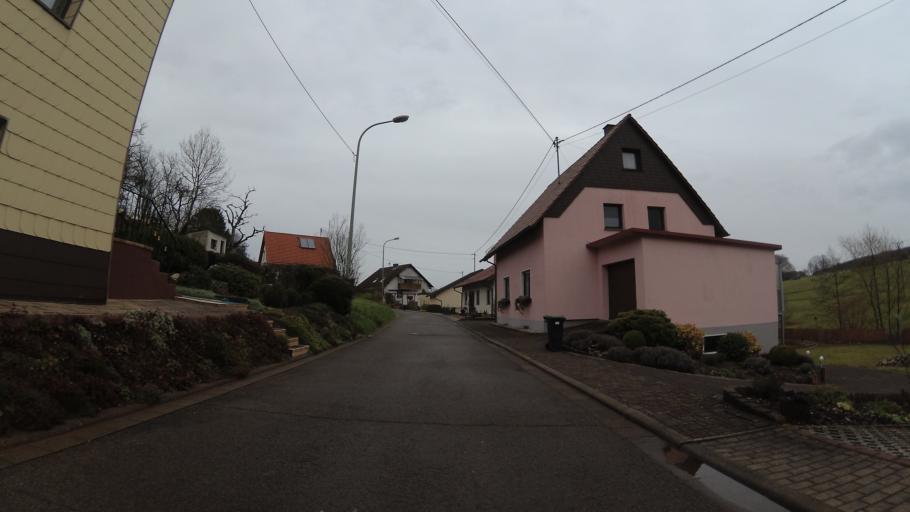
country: DE
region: Rheinland-Pfalz
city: Frohnhofen
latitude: 49.4520
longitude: 7.2959
